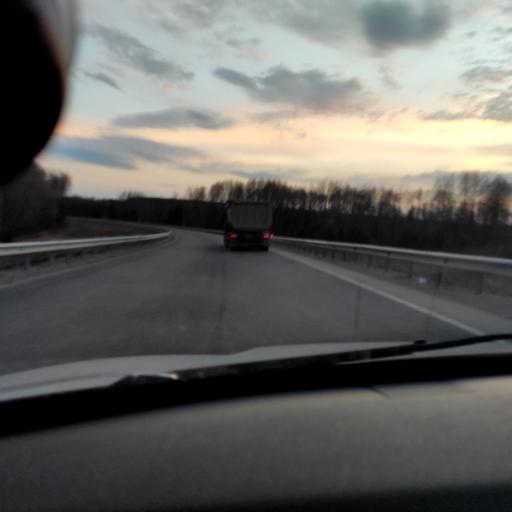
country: RU
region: Perm
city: Chusovoy
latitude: 58.3297
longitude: 57.7661
